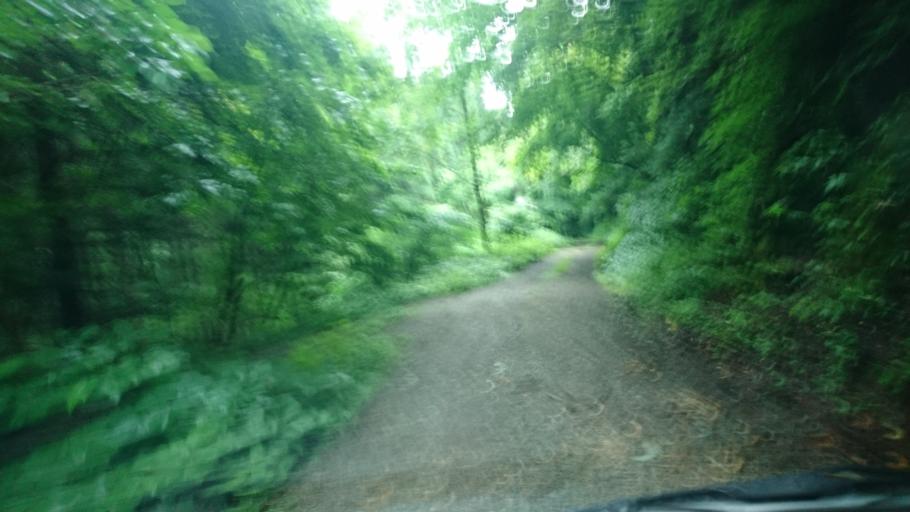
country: JP
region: Fukushima
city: Kitakata
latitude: 37.3436
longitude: 139.8145
